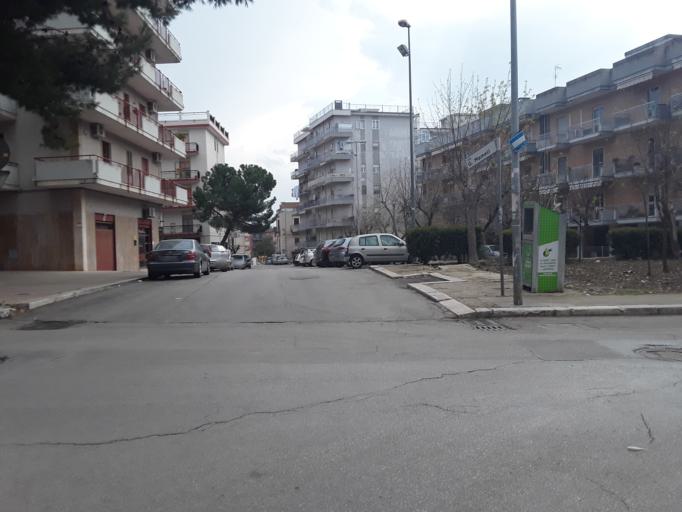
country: IT
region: Apulia
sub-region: Provincia di Bari
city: Ruvo di Puglia
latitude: 41.1198
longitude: 16.4790
